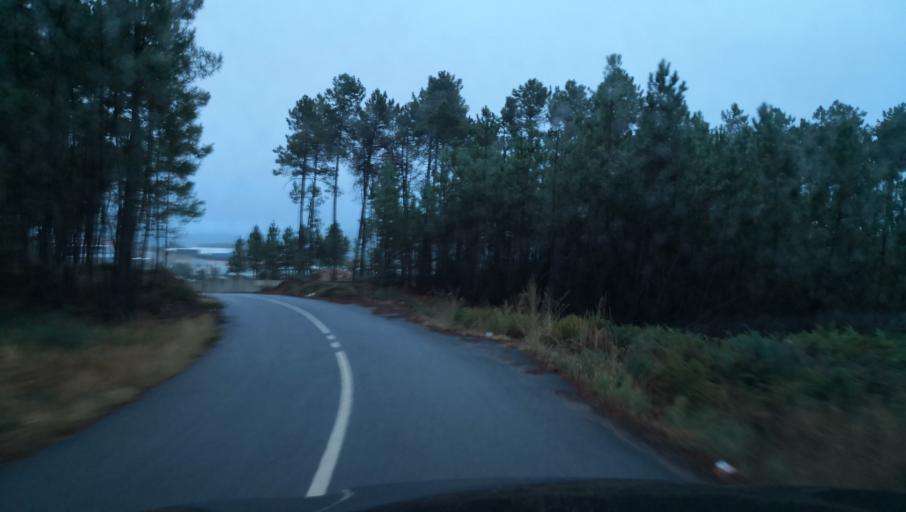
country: PT
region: Vila Real
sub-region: Sabrosa
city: Sabrosa
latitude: 41.2693
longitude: -7.5915
